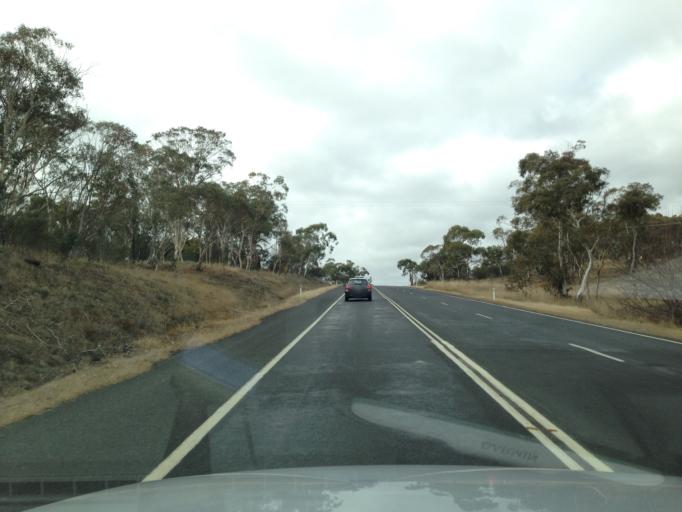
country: AU
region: New South Wales
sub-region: Cooma-Monaro
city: Cooma
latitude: -36.2406
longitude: 149.0719
